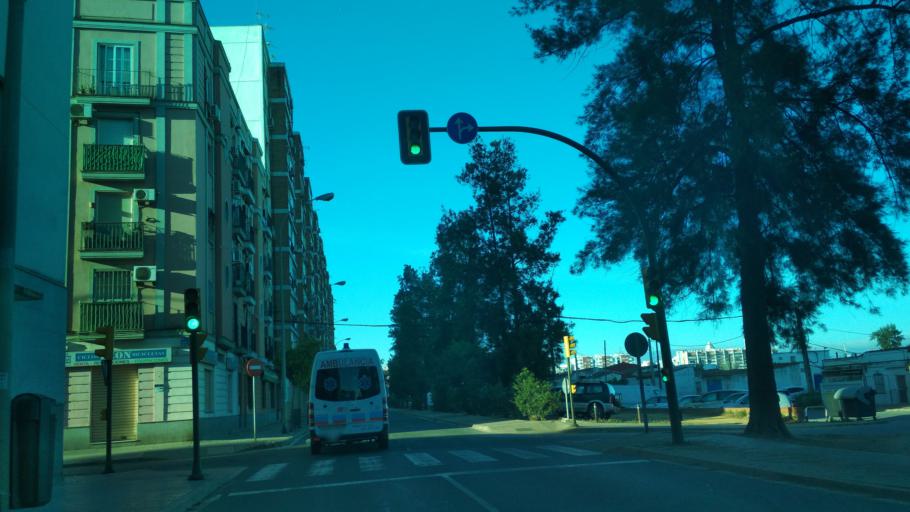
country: ES
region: Andalusia
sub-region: Provincia de Huelva
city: Huelva
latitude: 37.2727
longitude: -6.9503
